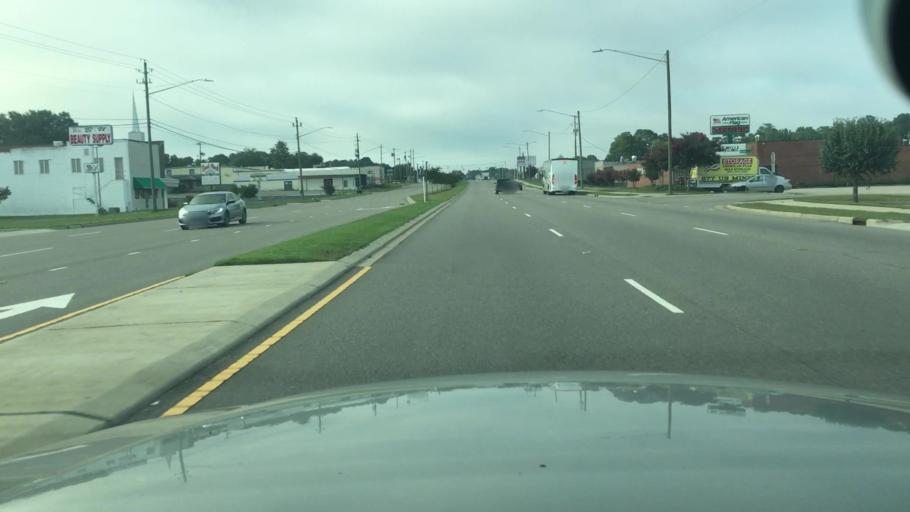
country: US
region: North Carolina
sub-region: Cumberland County
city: Fort Bragg
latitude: 35.0965
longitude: -78.9564
